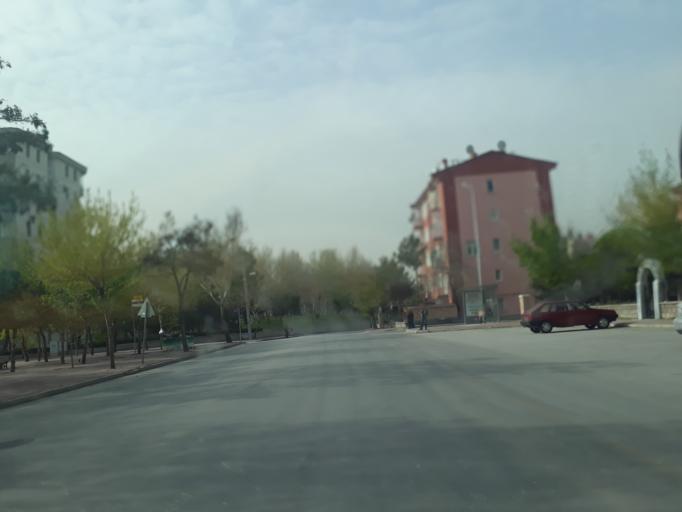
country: TR
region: Konya
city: Selcuklu
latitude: 37.9344
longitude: 32.4997
